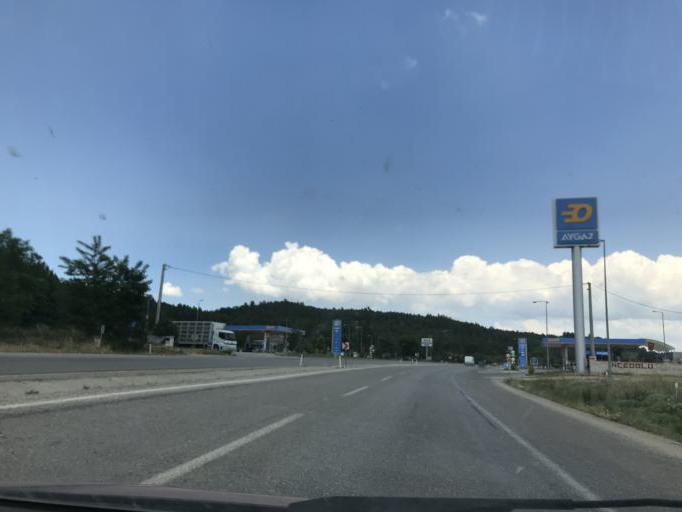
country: TR
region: Denizli
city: Tavas
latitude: 37.6134
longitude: 29.1425
